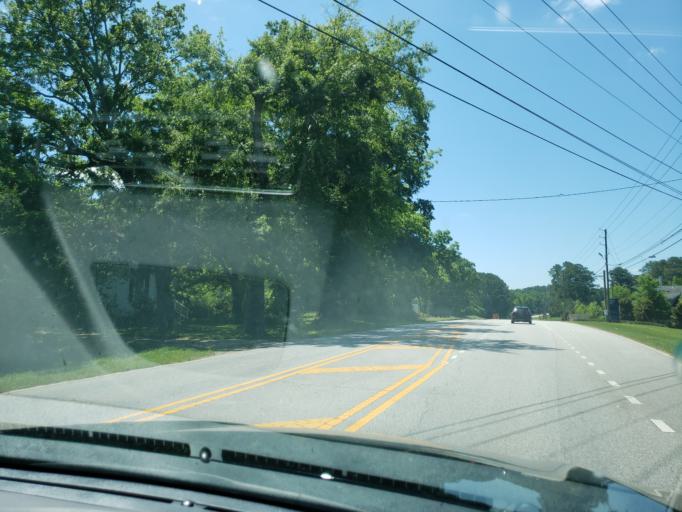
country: US
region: Alabama
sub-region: Lee County
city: Auburn
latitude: 32.6540
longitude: -85.4856
